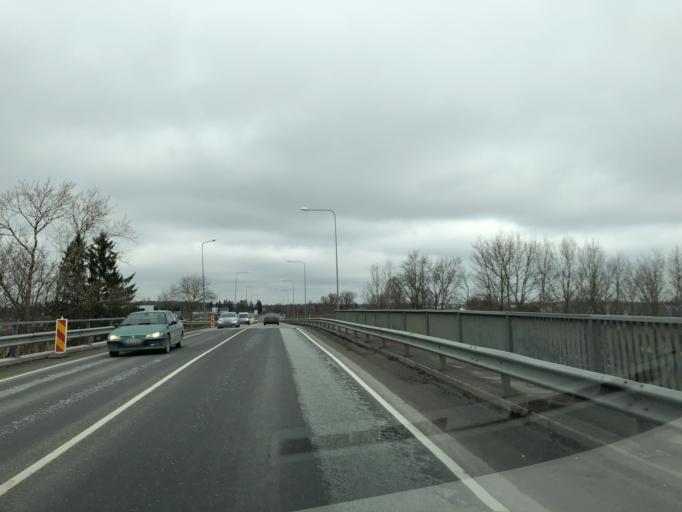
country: EE
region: Laeaene-Virumaa
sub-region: Rakvere linn
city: Rakvere
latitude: 59.3543
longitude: 26.3371
